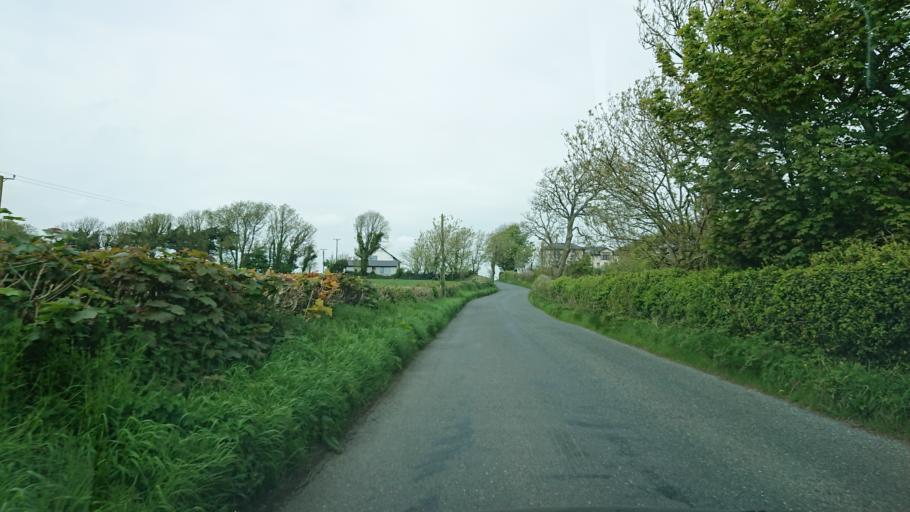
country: IE
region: Munster
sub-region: Waterford
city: Waterford
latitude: 52.2068
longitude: -7.0998
